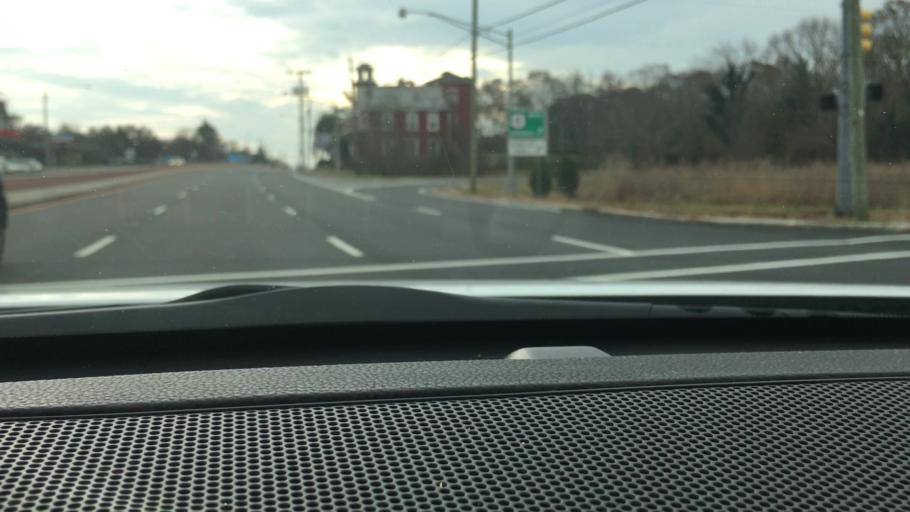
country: US
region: New Jersey
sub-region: Atlantic County
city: Absecon
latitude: 39.4273
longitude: -74.5045
